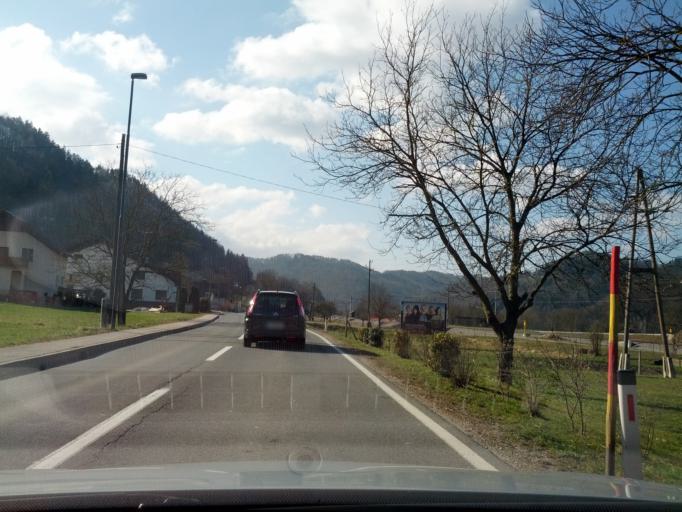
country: SI
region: Litija
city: Litija
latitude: 46.0779
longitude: 14.8257
